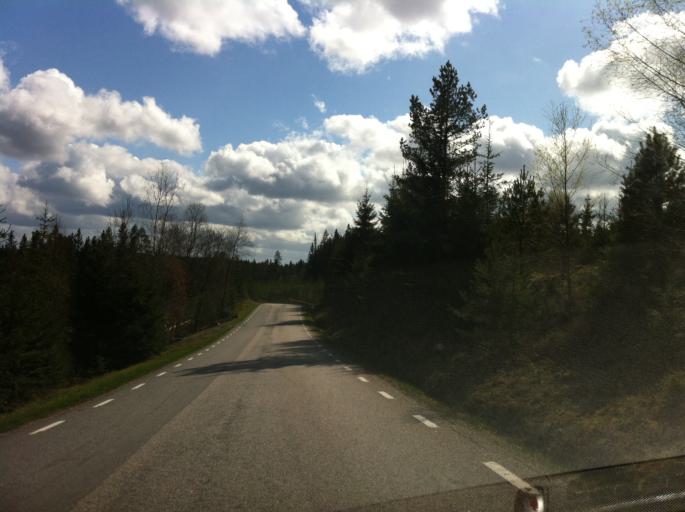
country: SE
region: Vaestra Goetaland
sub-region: Bollebygds Kommun
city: Bollebygd
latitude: 57.8112
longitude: 12.6396
